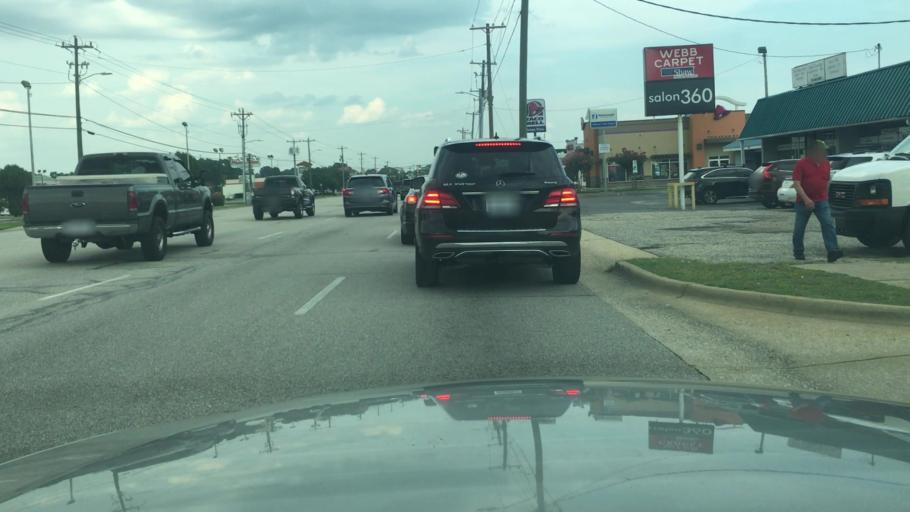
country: US
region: North Carolina
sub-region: Cumberland County
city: Fayetteville
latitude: 35.0451
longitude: -78.9271
